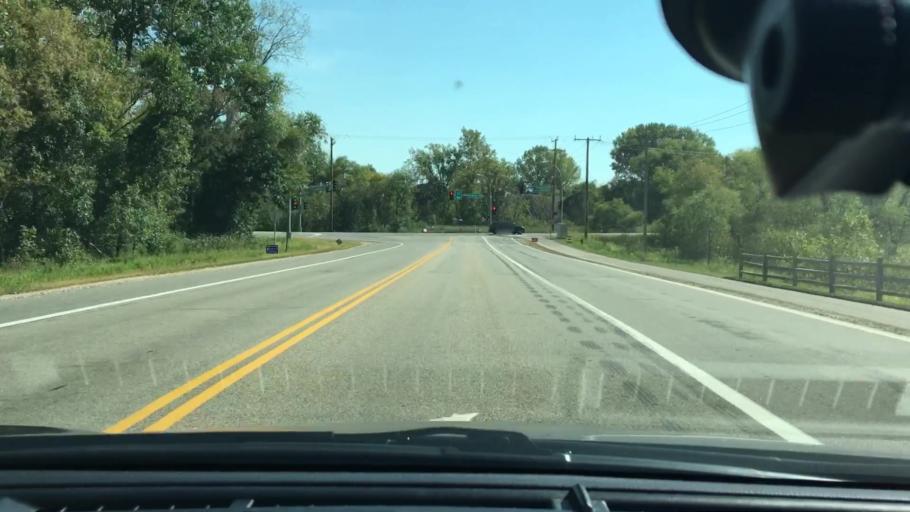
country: US
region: Minnesota
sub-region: Wright County
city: Hanover
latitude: 45.1620
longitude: -93.6673
